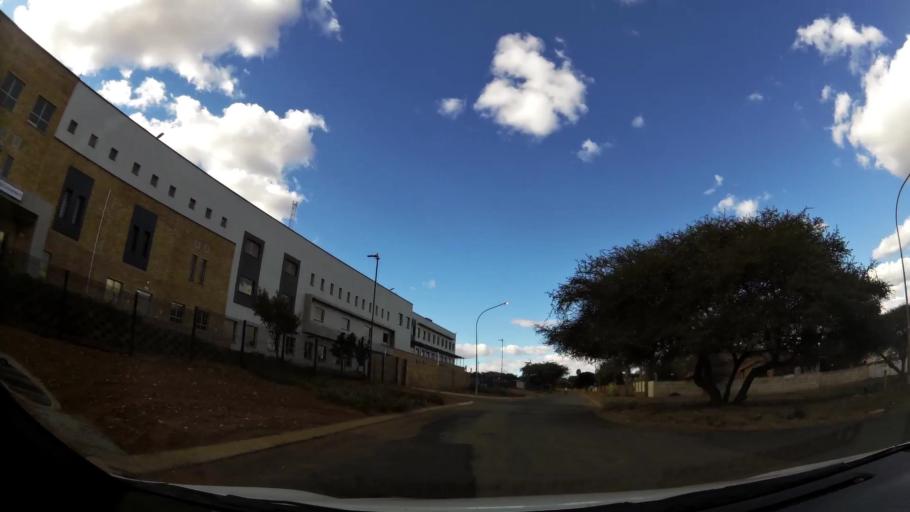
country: ZA
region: Limpopo
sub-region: Capricorn District Municipality
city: Polokwane
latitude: -23.9025
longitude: 29.4932
